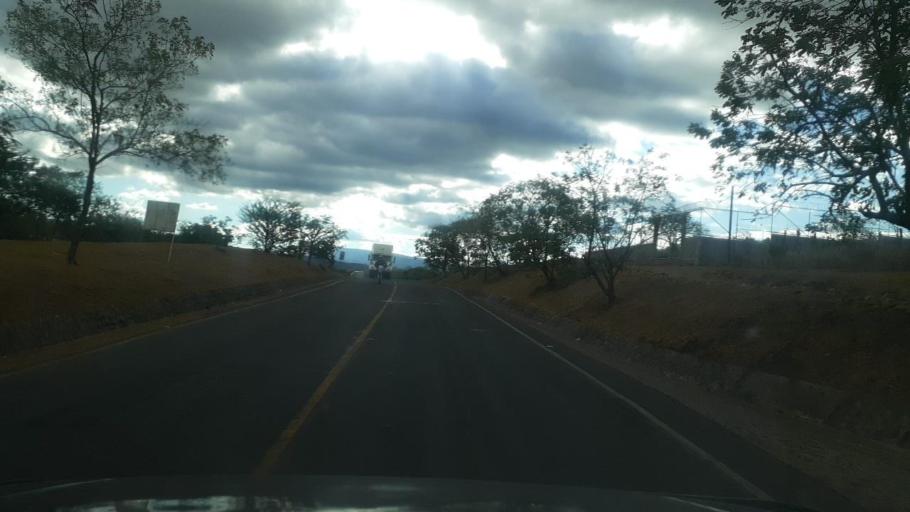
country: NI
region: Madriz
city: Somoto
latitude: 13.4744
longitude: -86.5995
